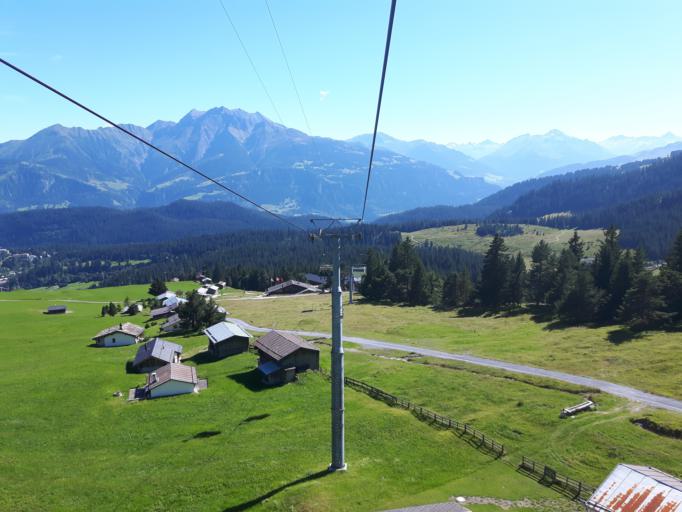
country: CH
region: Grisons
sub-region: Imboden District
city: Flims
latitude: 46.8497
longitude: 9.2677
